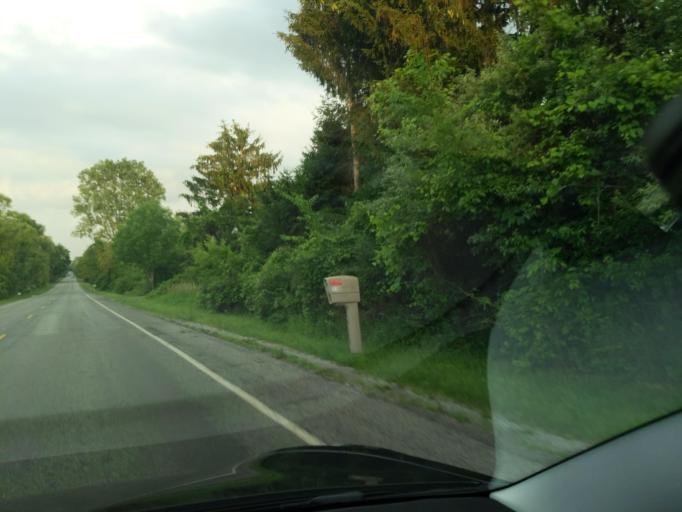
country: US
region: Michigan
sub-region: Ingham County
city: Mason
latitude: 42.5239
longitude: -84.4125
